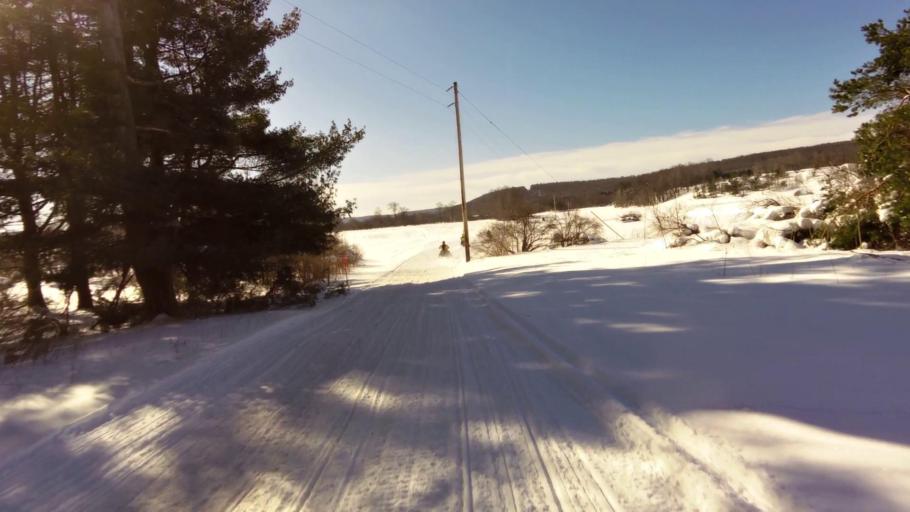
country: US
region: New York
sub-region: Cattaraugus County
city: Franklinville
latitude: 42.3691
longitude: -78.4649
